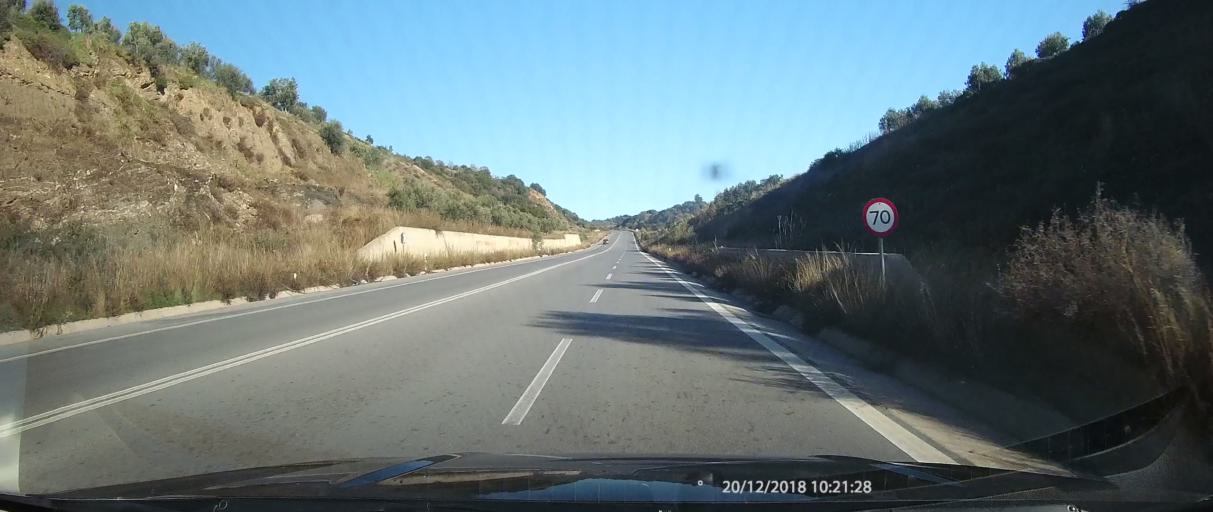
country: GR
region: Peloponnese
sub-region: Nomos Lakonias
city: Magoula
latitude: 37.1602
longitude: 22.4254
